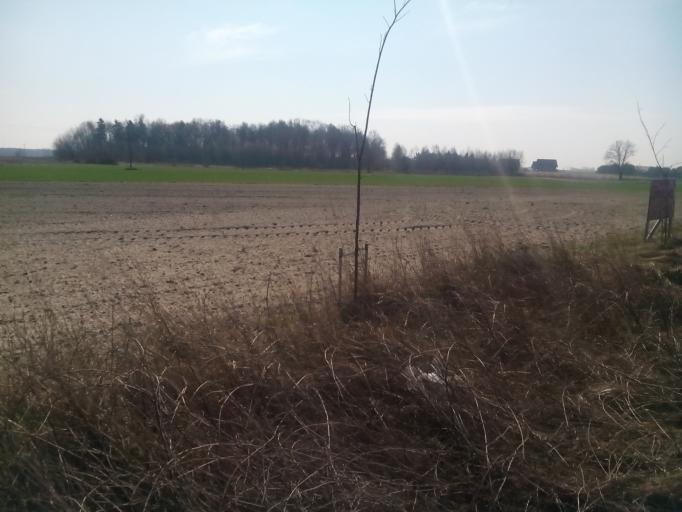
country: PL
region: Lower Silesian Voivodeship
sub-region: Powiat olesnicki
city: Dziadowa Kloda
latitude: 51.2307
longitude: 17.7002
